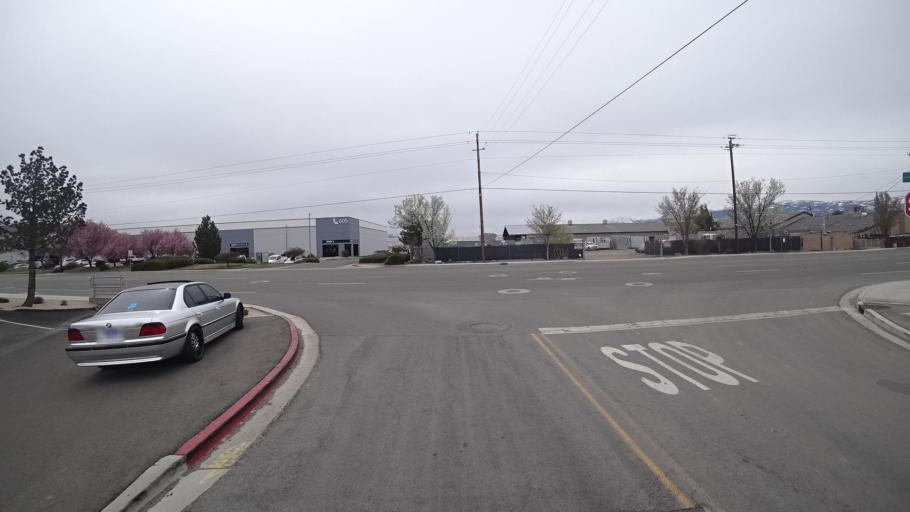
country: US
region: Nevada
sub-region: Washoe County
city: Sparks
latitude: 39.5276
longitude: -119.7527
